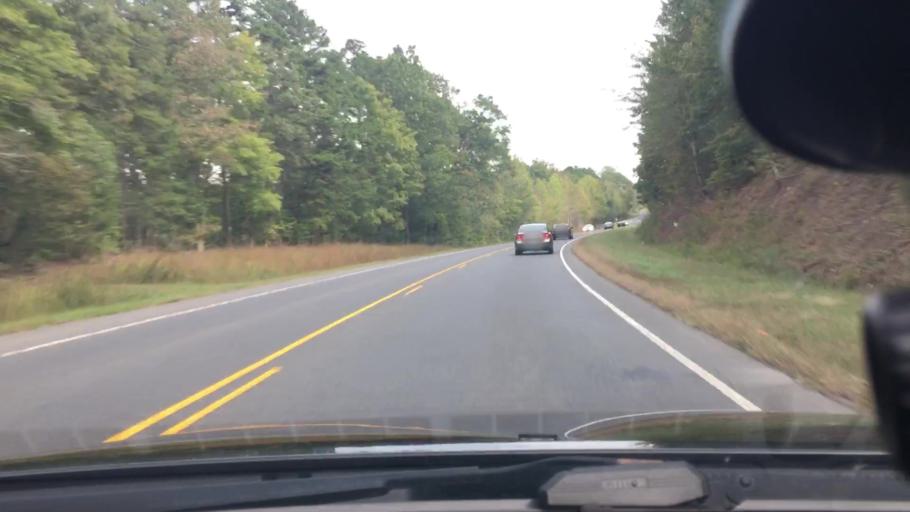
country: US
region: North Carolina
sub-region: Montgomery County
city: Mount Gilead
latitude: 35.3125
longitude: -80.0481
